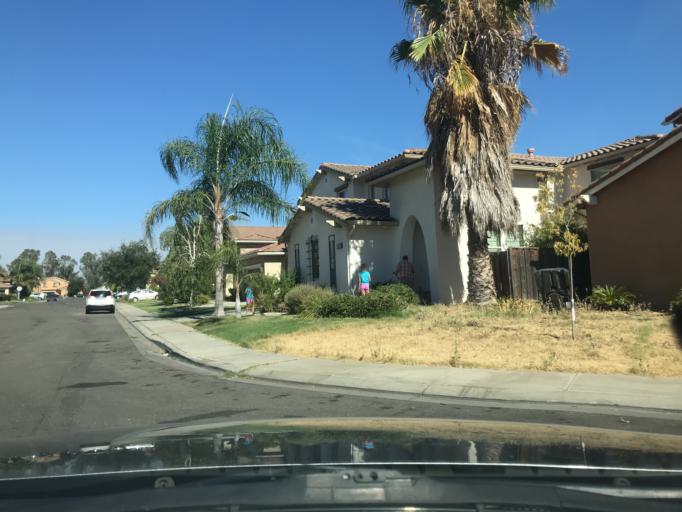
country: US
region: California
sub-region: Merced County
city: Atwater
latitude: 37.3470
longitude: -120.5699
